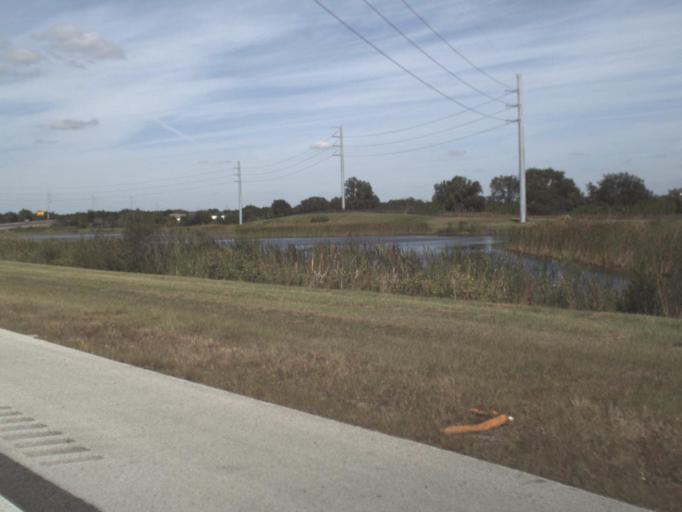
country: US
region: Florida
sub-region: Polk County
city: Citrus Ridge
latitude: 28.3224
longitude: -81.6122
